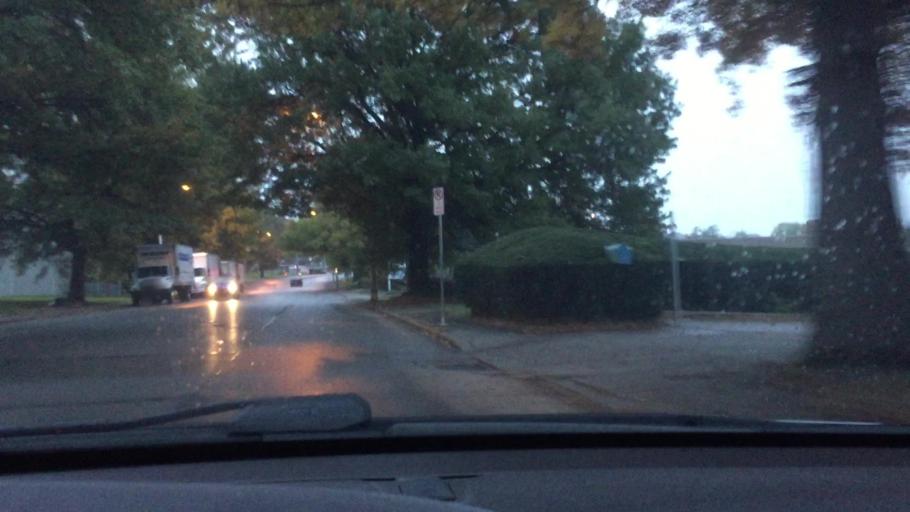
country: US
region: Pennsylvania
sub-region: Allegheny County
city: Ingram
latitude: 40.4424
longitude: -80.0819
